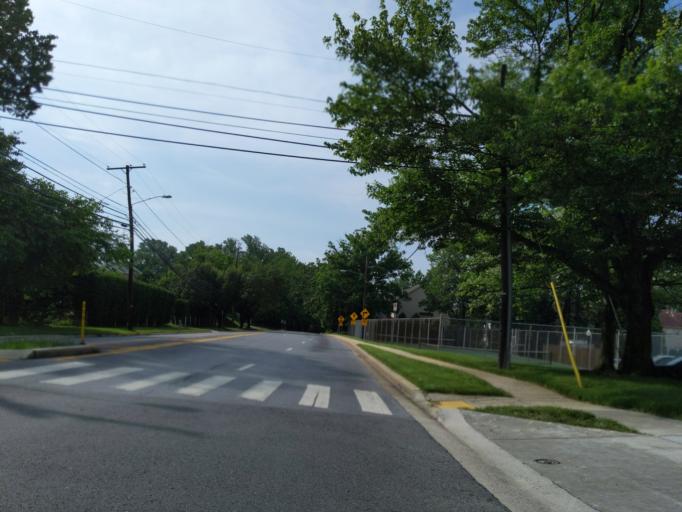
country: US
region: Maryland
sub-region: Montgomery County
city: Kemp Mill
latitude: 39.0375
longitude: -77.0267
